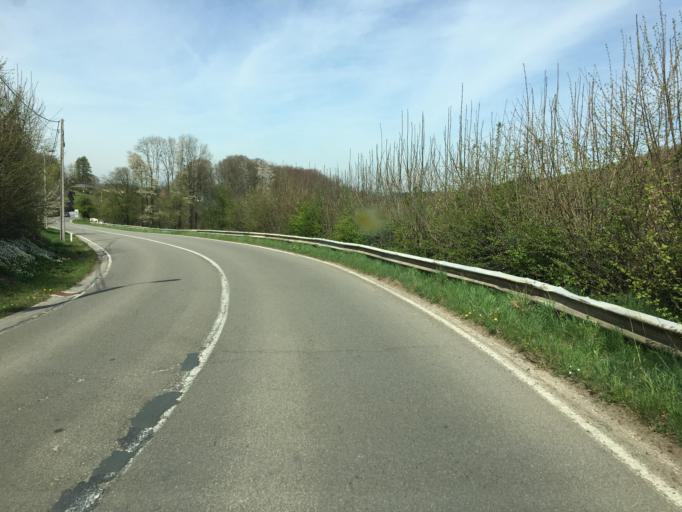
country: BE
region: Wallonia
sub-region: Province de Liege
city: Aywaille
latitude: 50.4265
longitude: 5.6808
